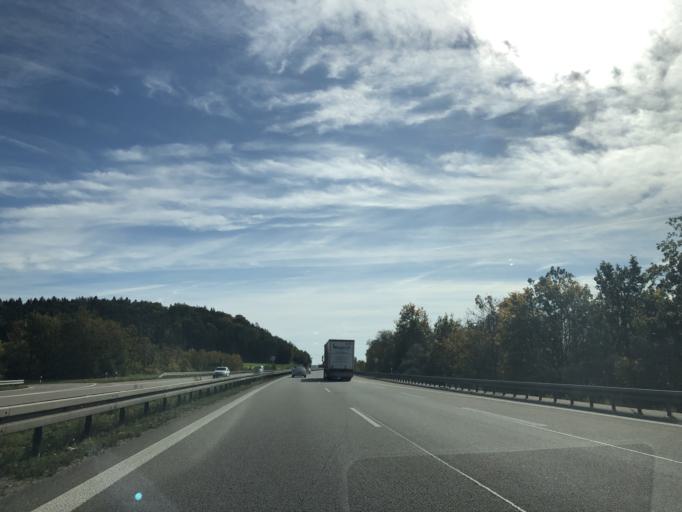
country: DE
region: Bavaria
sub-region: Upper Palatinate
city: Velburg
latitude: 49.2354
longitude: 11.6377
